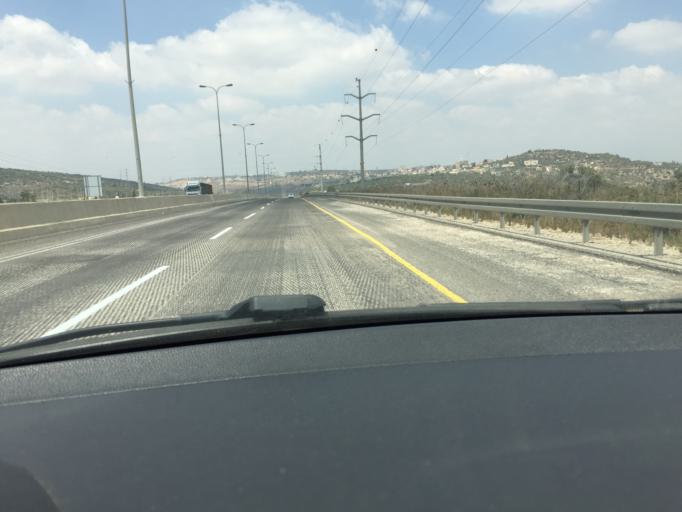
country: PS
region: West Bank
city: Kifil Haris
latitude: 32.1096
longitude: 35.1606
